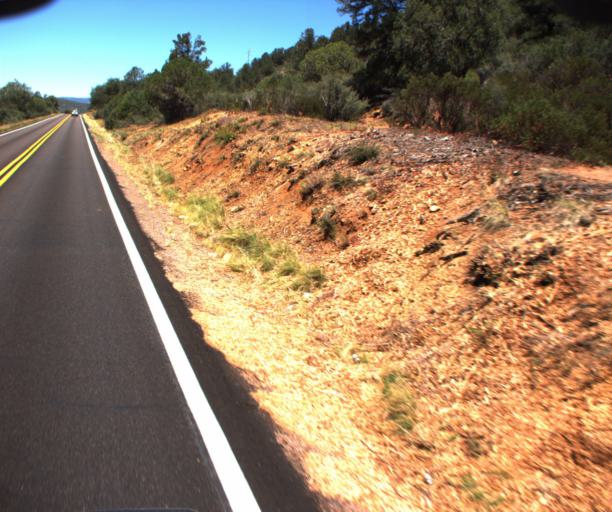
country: US
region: Arizona
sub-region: Gila County
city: Payson
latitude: 34.2868
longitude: -111.3401
